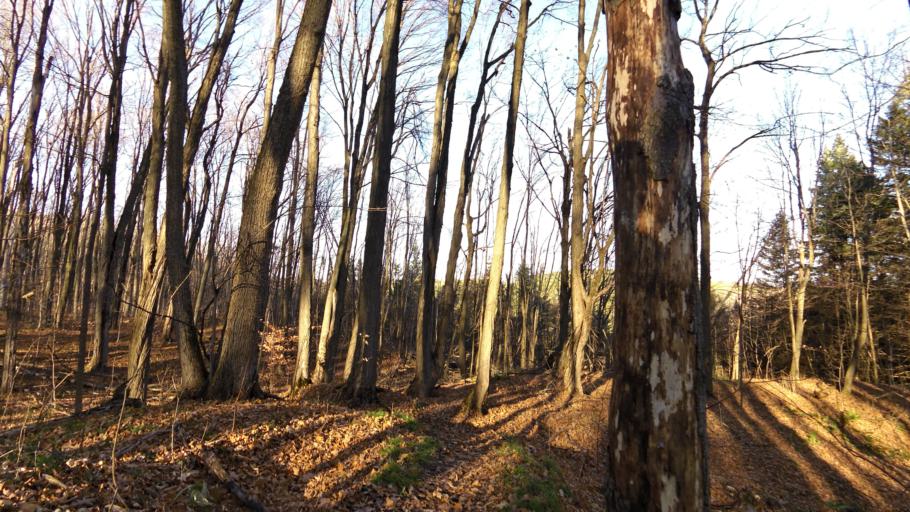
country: CA
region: Ontario
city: Orangeville
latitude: 43.9934
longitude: -80.0564
